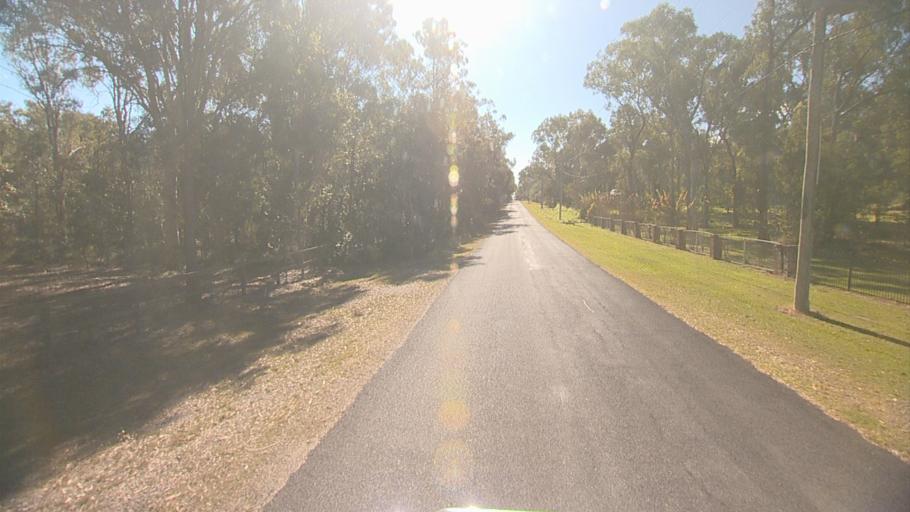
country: AU
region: Queensland
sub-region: Logan
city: Chambers Flat
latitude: -27.7436
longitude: 153.0939
